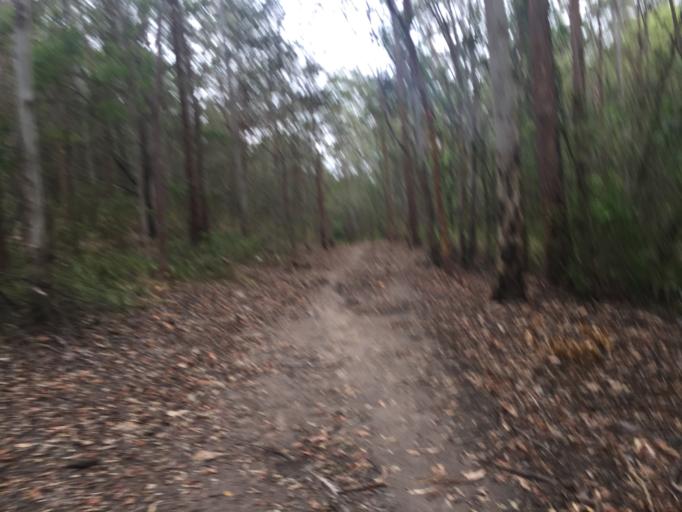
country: AU
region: Queensland
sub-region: Brisbane
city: Taringa
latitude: -27.4579
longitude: 152.9640
